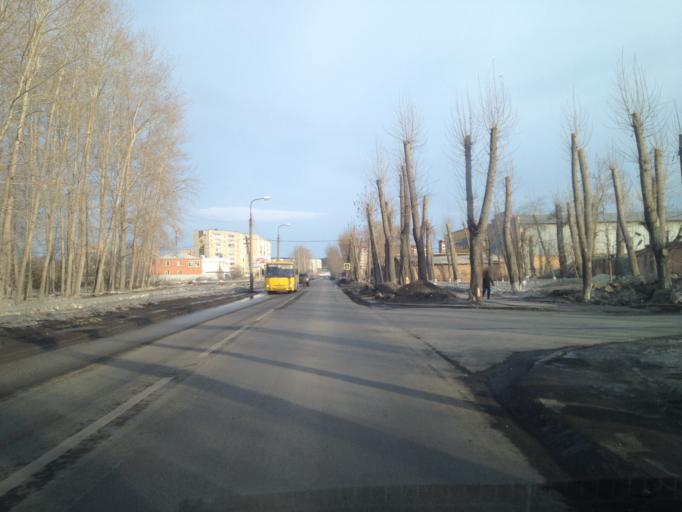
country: RU
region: Sverdlovsk
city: Sovkhoznyy
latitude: 56.7566
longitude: 60.5973
